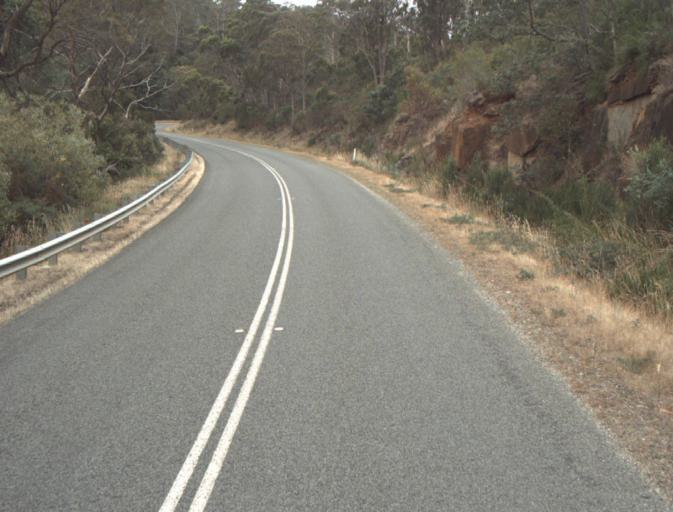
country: AU
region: Tasmania
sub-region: Northern Midlands
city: Evandale
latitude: -41.4940
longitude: 147.4253
